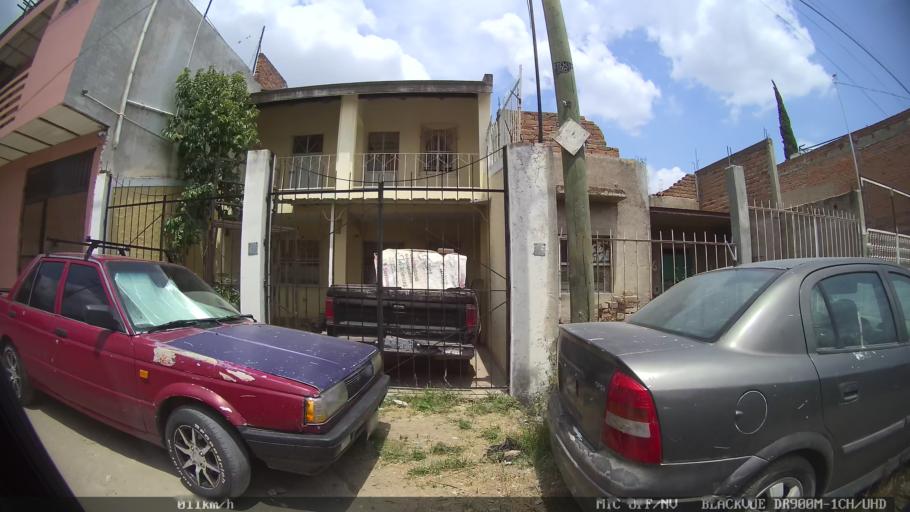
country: MX
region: Jalisco
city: Tonala
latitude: 20.6782
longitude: -103.2364
